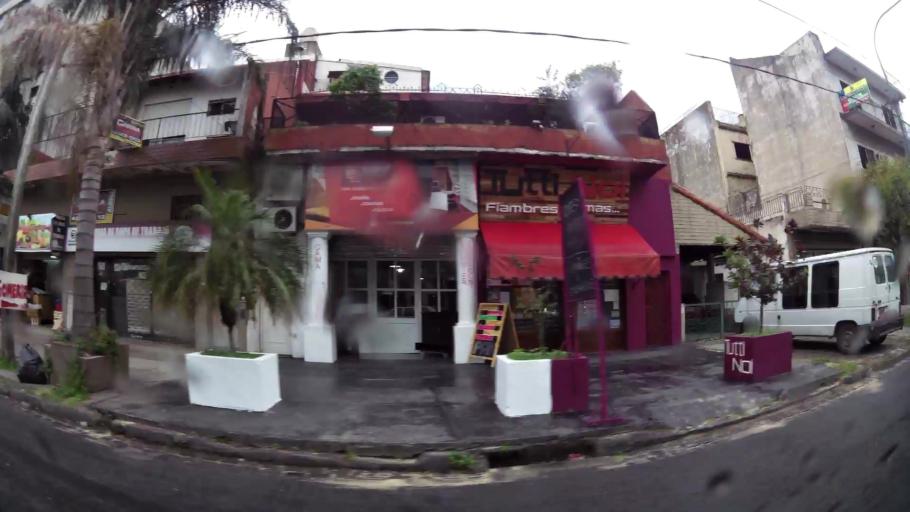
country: AR
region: Buenos Aires
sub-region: Partido de Lanus
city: Lanus
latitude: -34.6860
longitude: -58.4050
